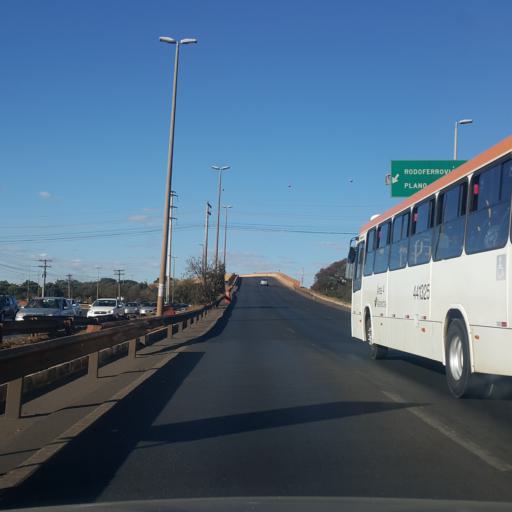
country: BR
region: Federal District
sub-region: Brasilia
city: Brasilia
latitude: -15.7863
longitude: -47.9437
